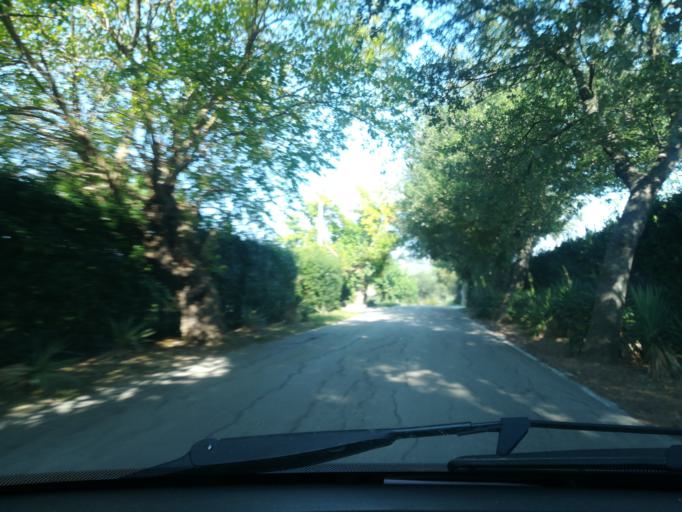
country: IT
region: The Marches
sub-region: Provincia di Macerata
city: Macerata
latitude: 43.2692
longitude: 13.4511
